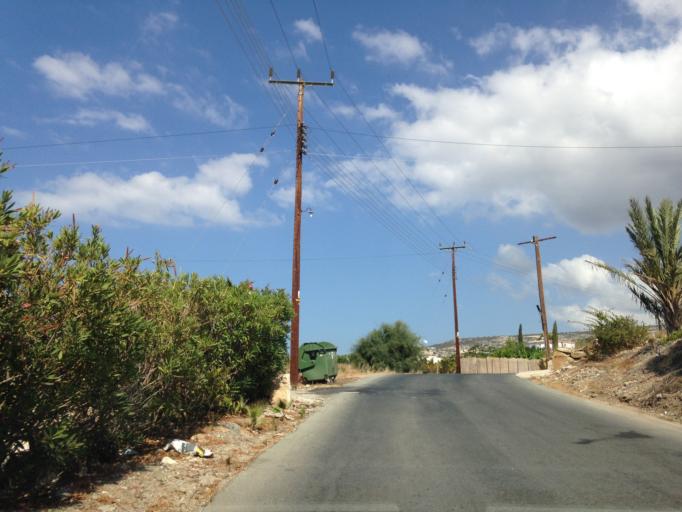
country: CY
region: Pafos
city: Pegeia
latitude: 34.8685
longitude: 32.3734
